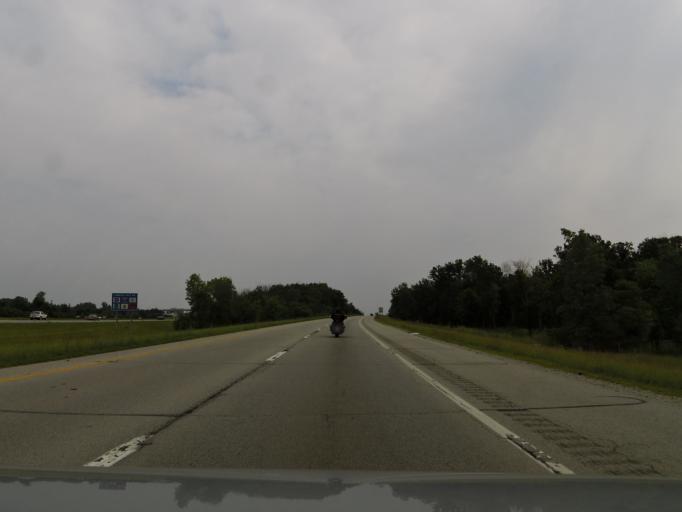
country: US
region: Ohio
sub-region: Warren County
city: Five Points
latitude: 39.6151
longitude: -84.2314
